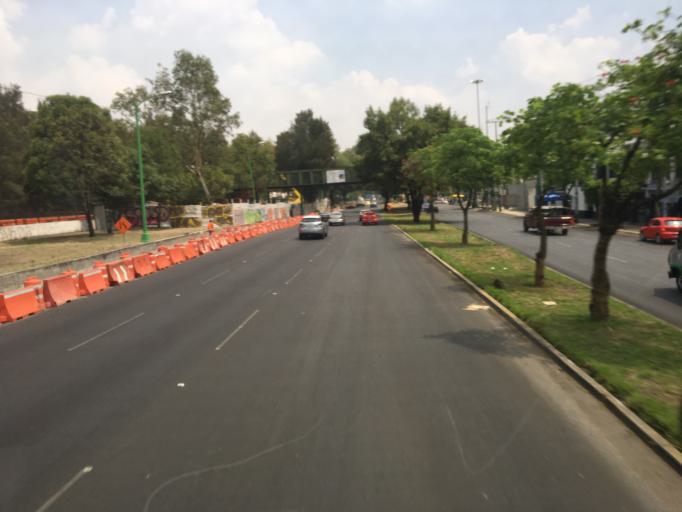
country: MX
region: Mexico
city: Colonia Lindavista
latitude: 19.4981
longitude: -99.1478
